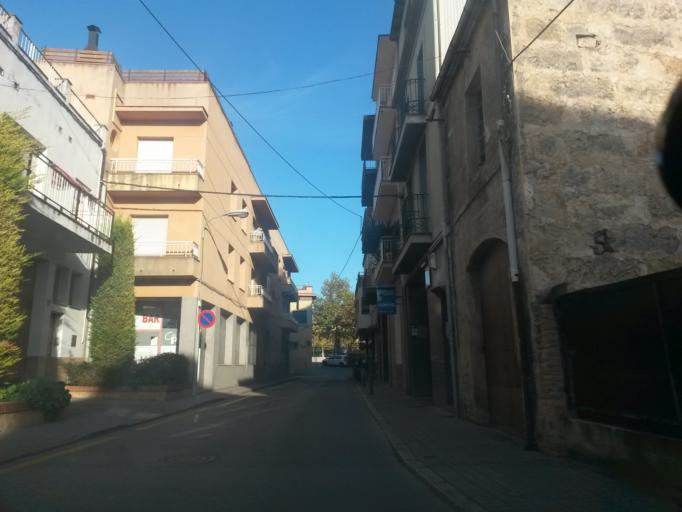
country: ES
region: Catalonia
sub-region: Provincia de Girona
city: Banyoles
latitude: 42.1177
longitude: 2.7604
